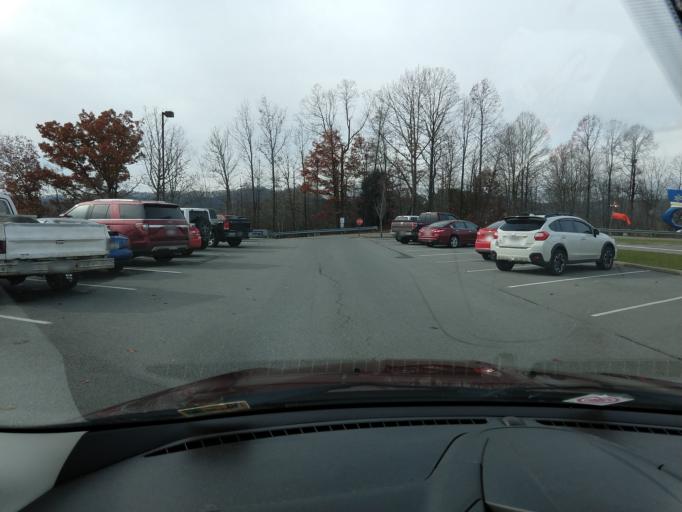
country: US
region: West Virginia
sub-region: Nicholas County
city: Summersville
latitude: 38.2924
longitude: -80.8312
